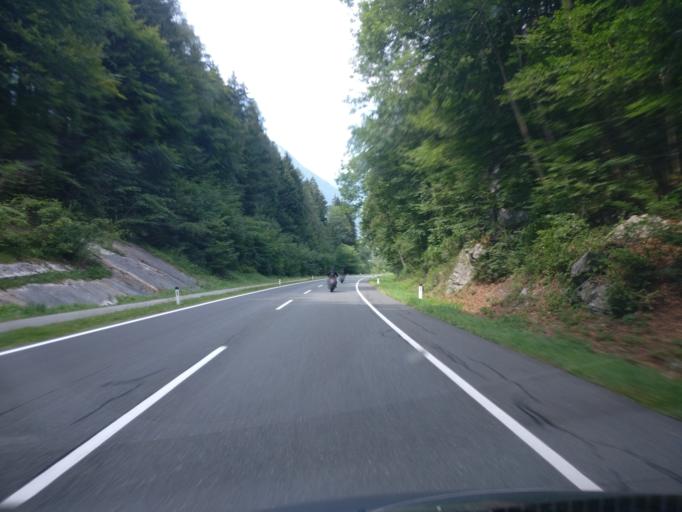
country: AT
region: Salzburg
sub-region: Politischer Bezirk Hallein
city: Scheffau am Tennengebirge
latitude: 47.5785
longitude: 13.1910
